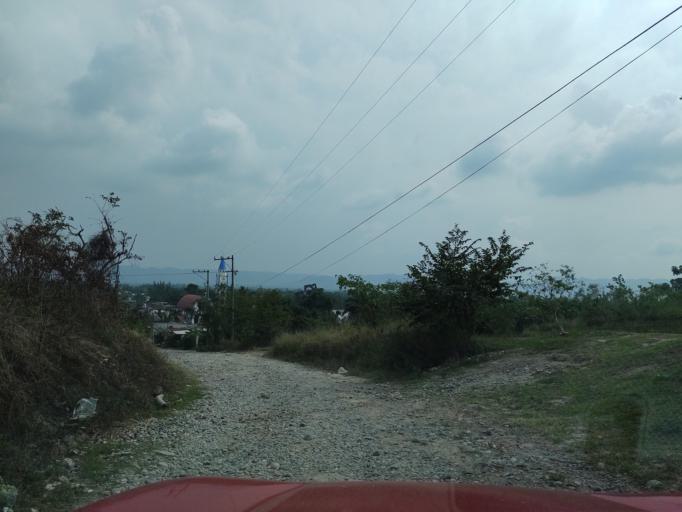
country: MX
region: Veracruz
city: Agua Dulce
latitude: 20.3634
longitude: -97.2967
